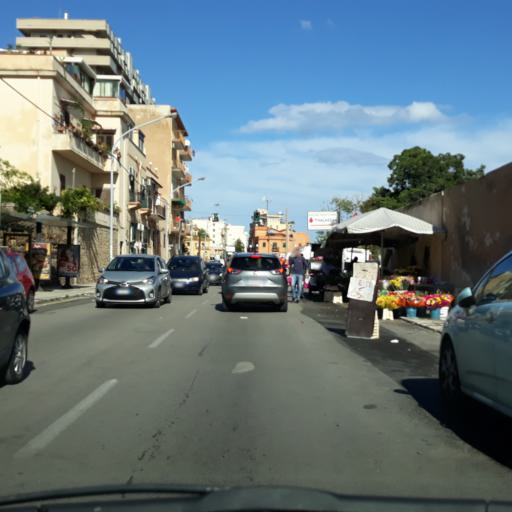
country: IT
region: Sicily
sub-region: Palermo
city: Palermo
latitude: 38.1461
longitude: 13.3701
